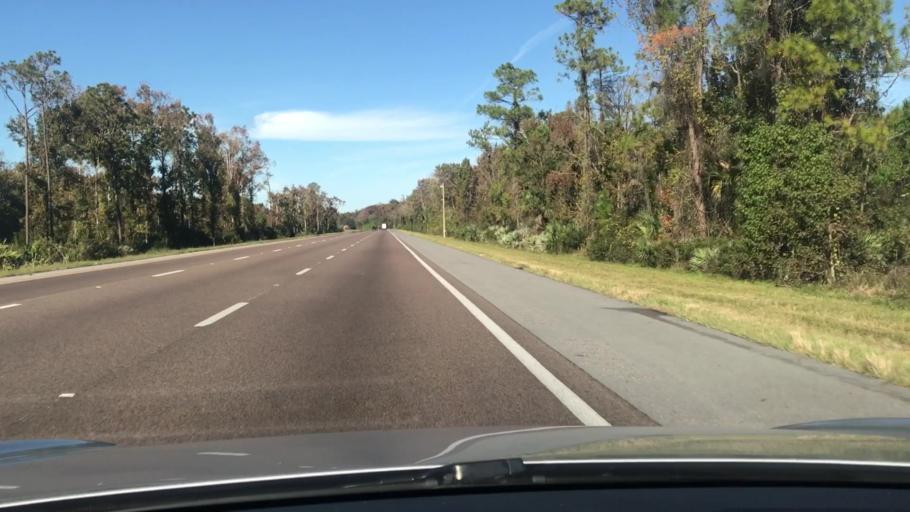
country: US
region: Florida
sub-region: Volusia County
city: Edgewater
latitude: 28.9207
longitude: -80.9371
